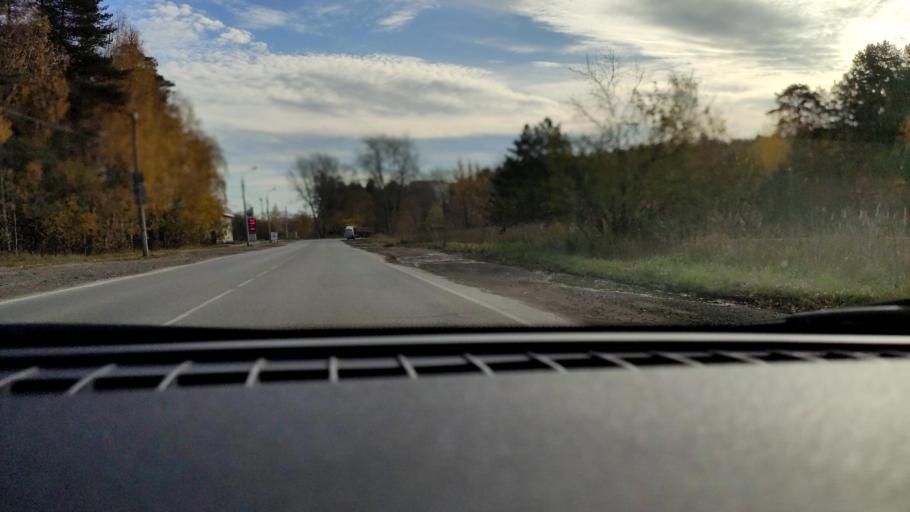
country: RU
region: Perm
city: Overyata
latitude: 58.0130
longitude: 55.9200
